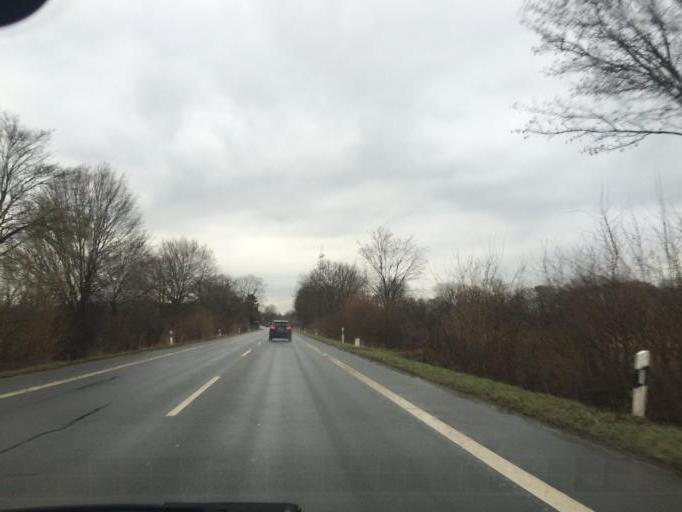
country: DE
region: North Rhine-Westphalia
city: Dorsten
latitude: 51.6270
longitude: 6.9563
